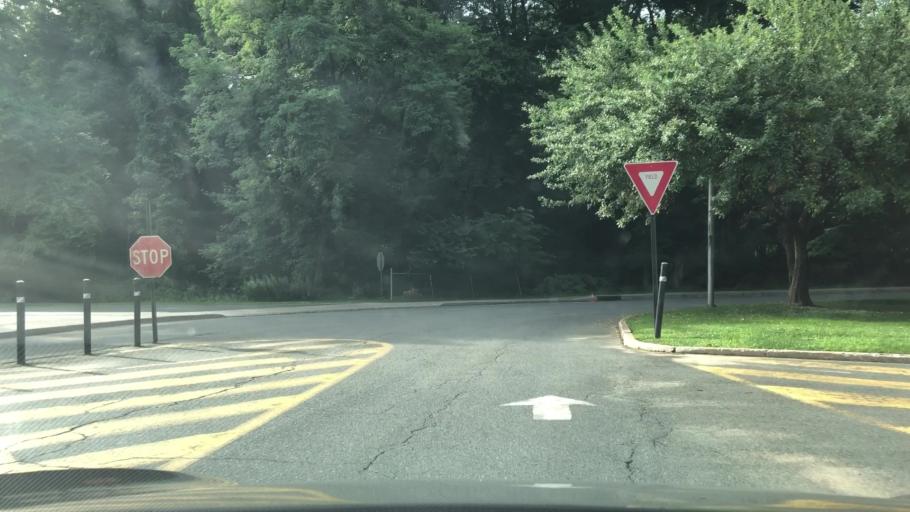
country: US
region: New Jersey
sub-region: Mercer County
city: Lawrenceville
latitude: 40.2725
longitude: -74.7398
